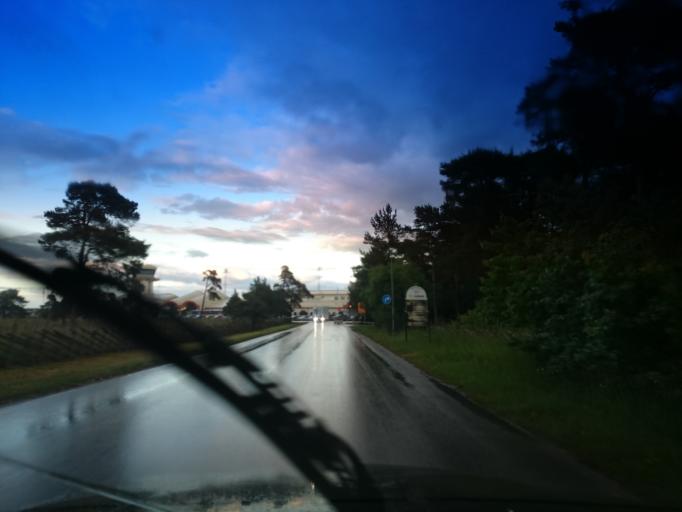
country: SE
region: Gotland
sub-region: Gotland
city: Visby
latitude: 57.6606
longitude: 18.3357
